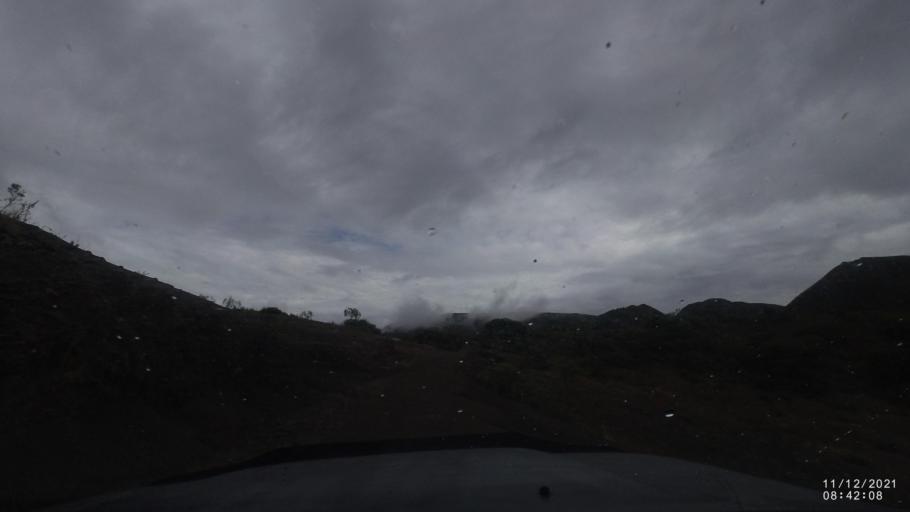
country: BO
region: Cochabamba
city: Tarata
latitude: -17.9170
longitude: -65.9353
